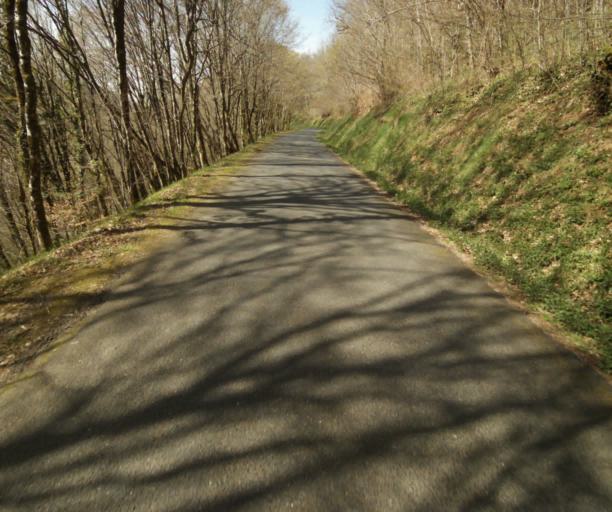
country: FR
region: Limousin
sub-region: Departement de la Correze
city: Naves
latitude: 45.3432
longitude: 1.7823
